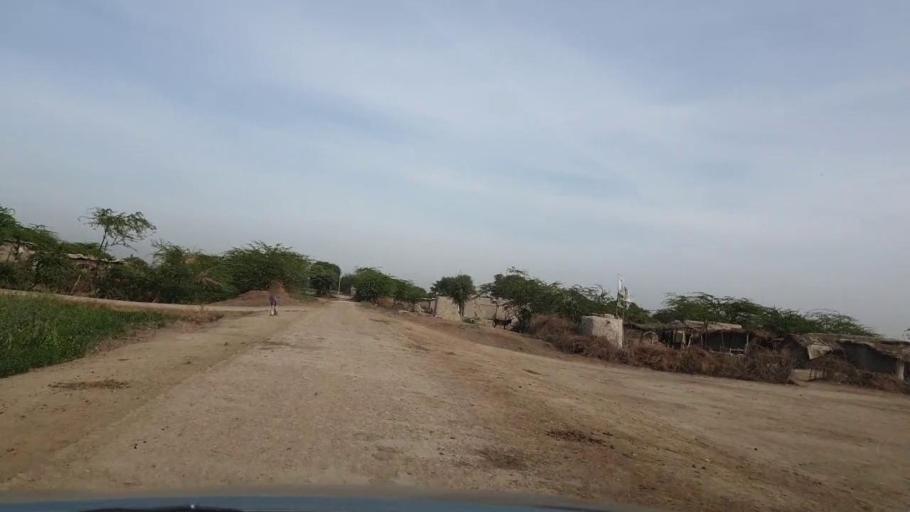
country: PK
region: Sindh
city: Kunri
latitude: 25.1649
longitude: 69.6224
